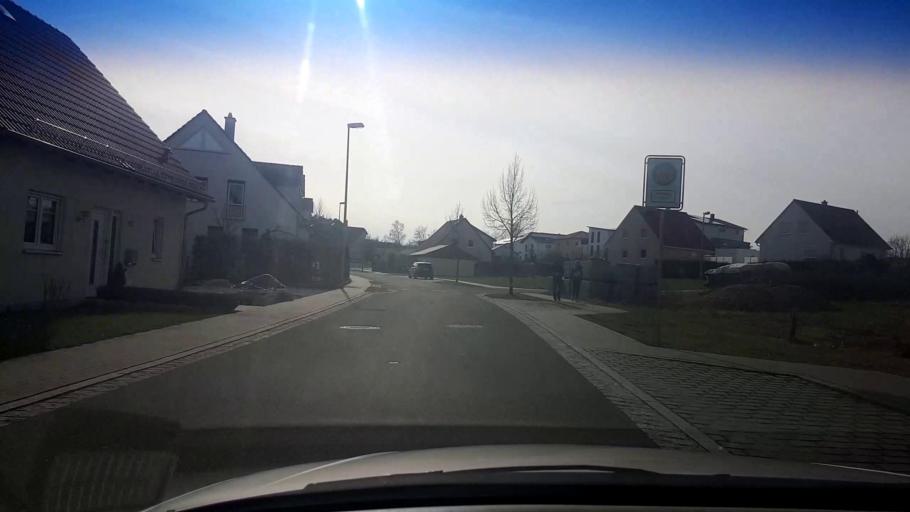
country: DE
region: Bavaria
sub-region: Upper Franconia
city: Burgebrach
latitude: 49.8211
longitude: 10.7409
